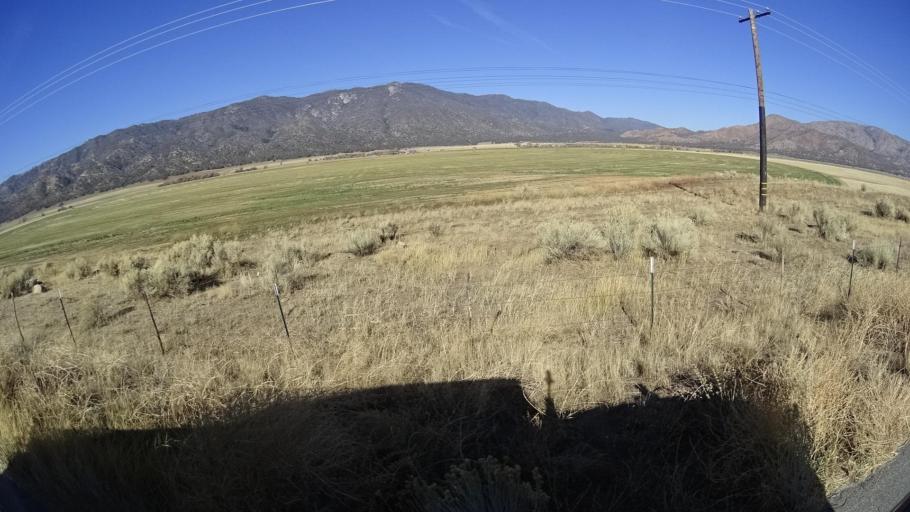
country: US
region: California
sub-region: Kern County
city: Bodfish
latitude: 35.3961
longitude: -118.5239
